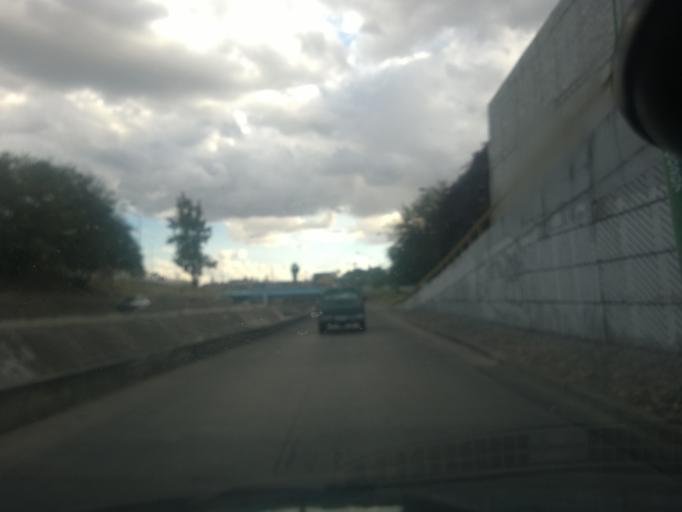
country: MX
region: Guanajuato
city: Leon
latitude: 21.1420
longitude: -101.6805
